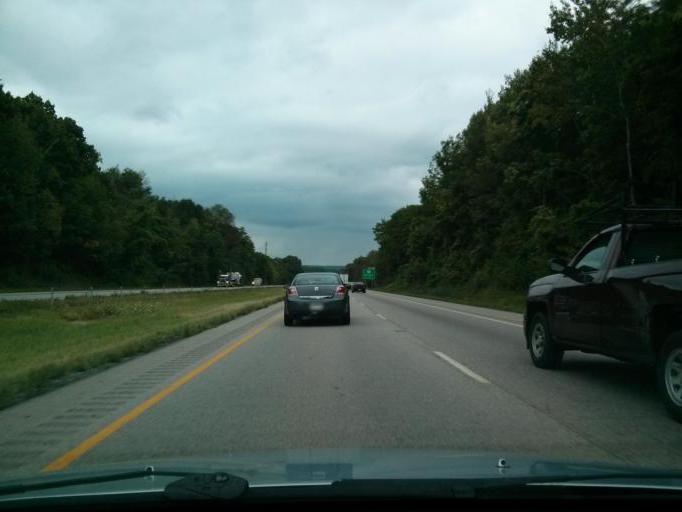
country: US
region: Ohio
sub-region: Mahoning County
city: Craig Beach
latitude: 41.1059
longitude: -81.0671
